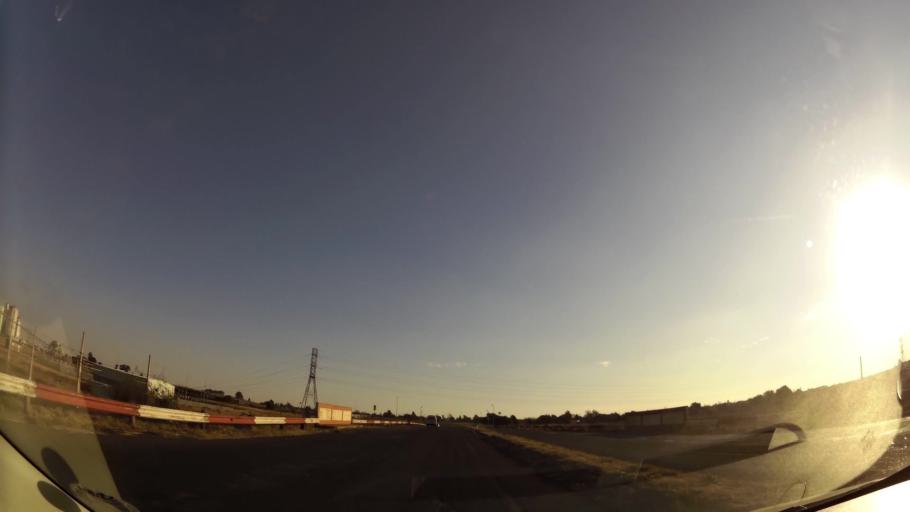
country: ZA
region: Gauteng
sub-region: West Rand District Municipality
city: Randfontein
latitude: -26.2052
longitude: 27.6632
